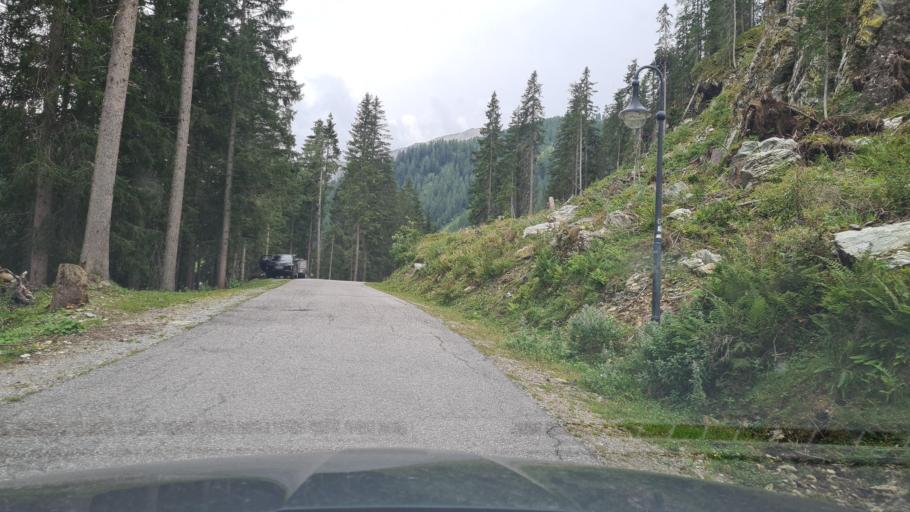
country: AT
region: Salzburg
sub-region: Politischer Bezirk Sankt Johann im Pongau
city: Untertauern
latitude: 47.2975
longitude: 13.4552
